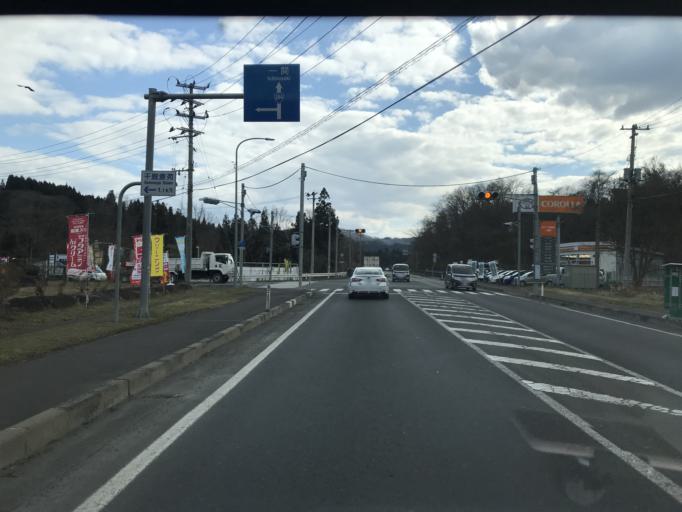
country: JP
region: Iwate
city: Ichinoseki
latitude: 38.9070
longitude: 141.3260
